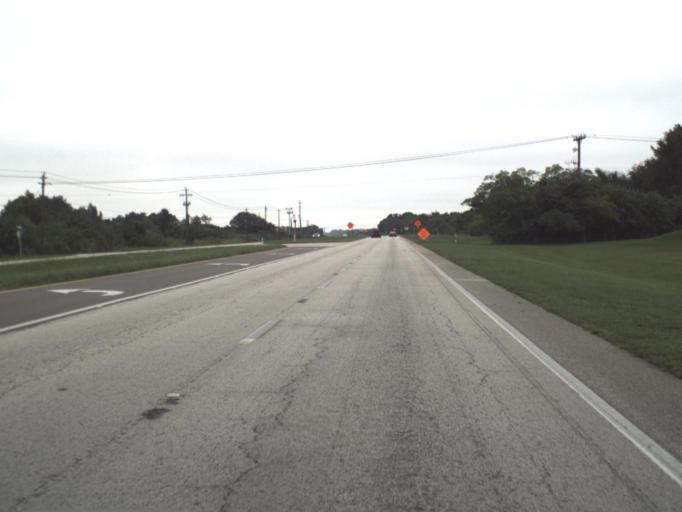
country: US
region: Florida
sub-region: Manatee County
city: Memphis
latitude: 27.5931
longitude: -82.5397
